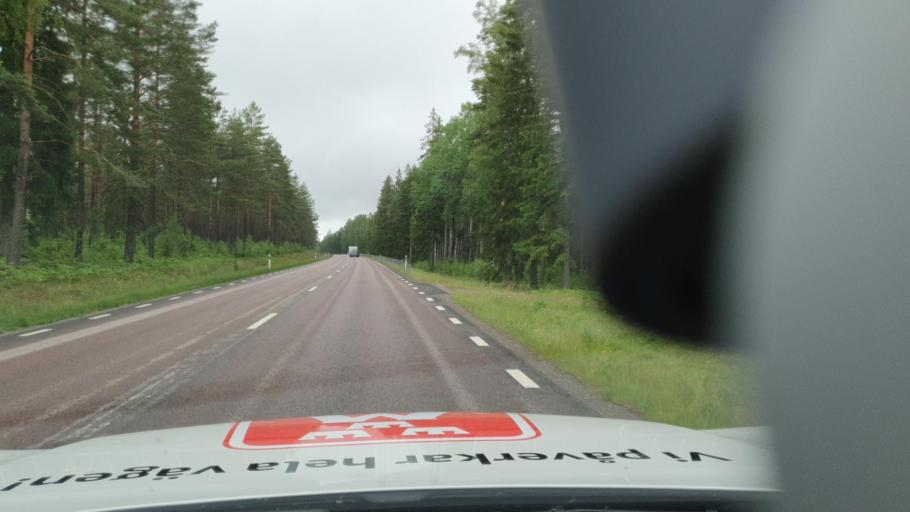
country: SE
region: Vaermland
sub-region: Kristinehamns Kommun
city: Bjorneborg
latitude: 59.1931
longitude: 14.1828
